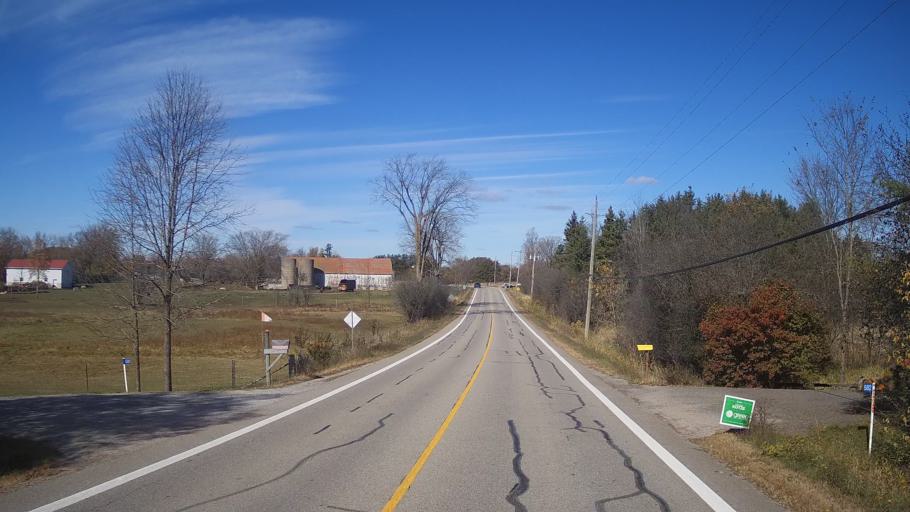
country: CA
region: Ontario
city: Perth
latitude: 44.8789
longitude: -76.3047
